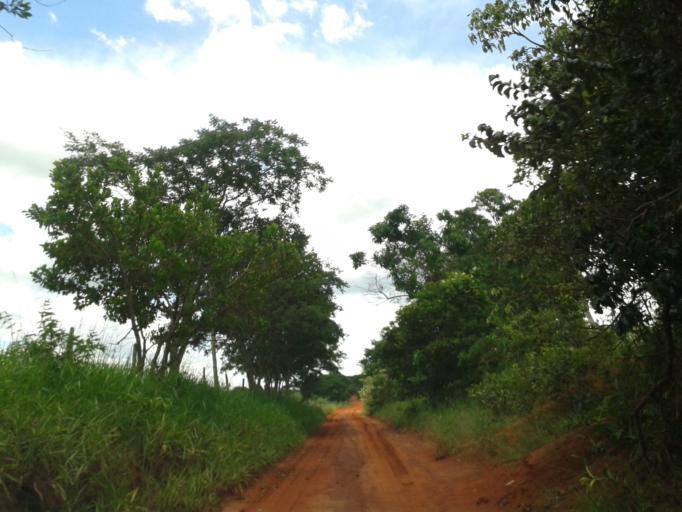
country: BR
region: Minas Gerais
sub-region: Ituiutaba
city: Ituiutaba
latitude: -18.8476
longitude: -49.5147
